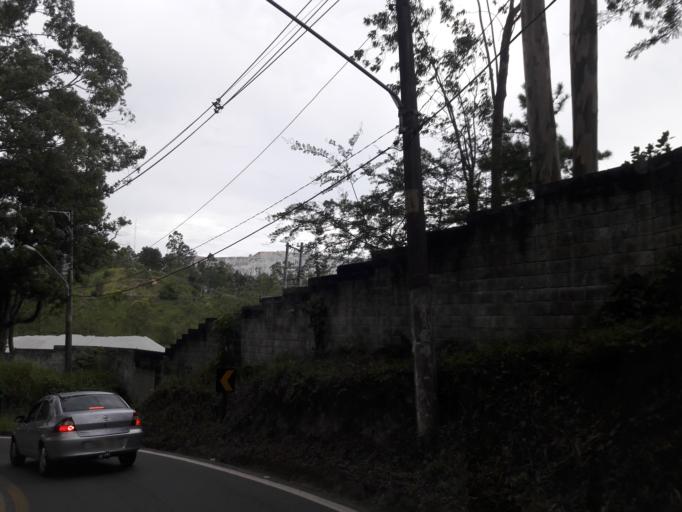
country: BR
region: Sao Paulo
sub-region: Aruja
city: Aruja
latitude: -23.3552
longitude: -46.4230
